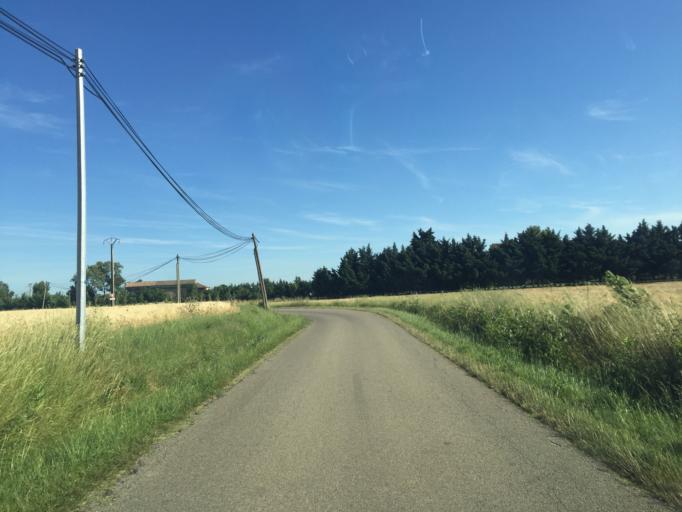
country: FR
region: Provence-Alpes-Cote d'Azur
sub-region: Departement du Vaucluse
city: Caderousse
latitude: 44.1125
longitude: 4.7410
